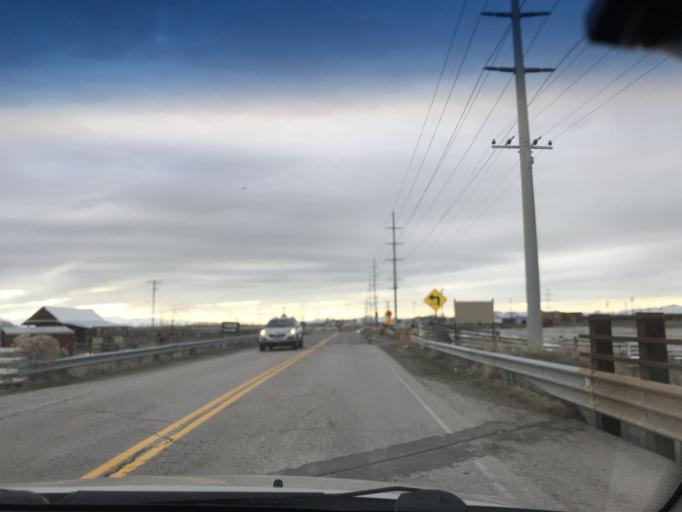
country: US
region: Utah
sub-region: Davis County
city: North Salt Lake
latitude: 40.8420
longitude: -111.9536
